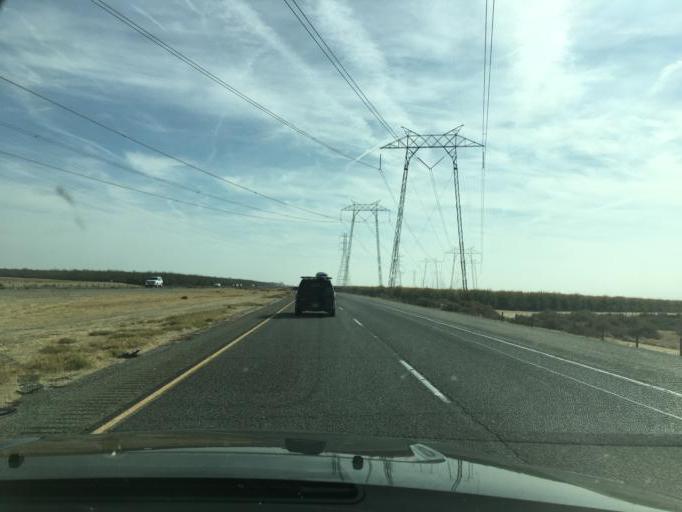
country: US
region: California
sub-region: Kern County
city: Buttonwillow
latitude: 35.4943
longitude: -119.5287
